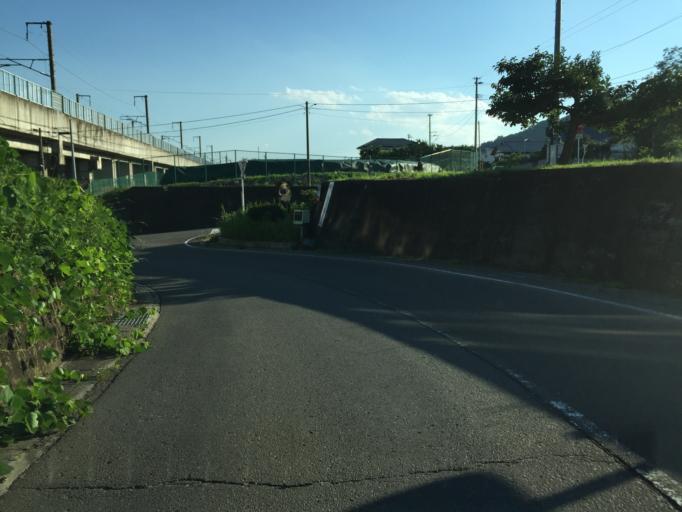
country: JP
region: Fukushima
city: Hobaramachi
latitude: 37.8606
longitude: 140.5210
